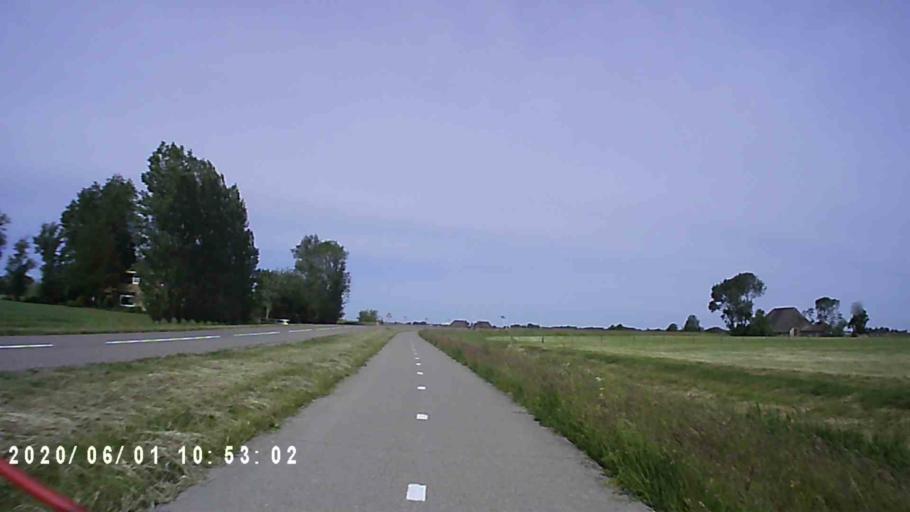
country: NL
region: Friesland
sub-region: Gemeente Franekeradeel
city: Franeker
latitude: 53.2012
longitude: 5.5152
